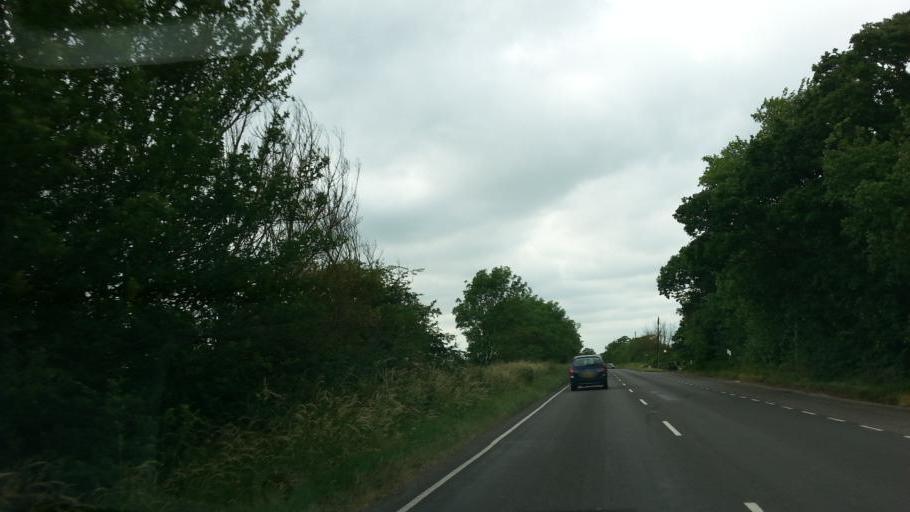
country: GB
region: England
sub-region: Cambridgeshire
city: Papworth Everard
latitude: 52.2310
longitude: -0.1047
